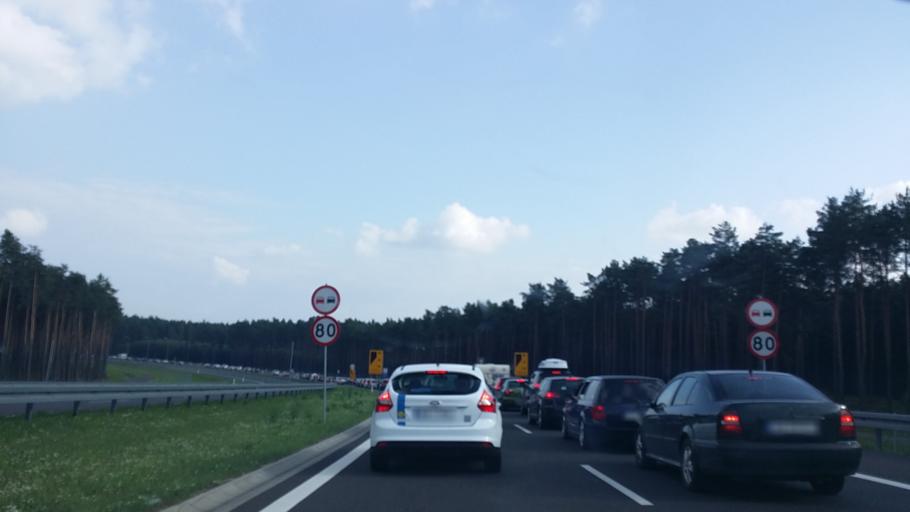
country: PL
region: Lubusz
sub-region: Powiat miedzyrzecki
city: Miedzyrzecz
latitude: 52.4758
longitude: 15.5530
